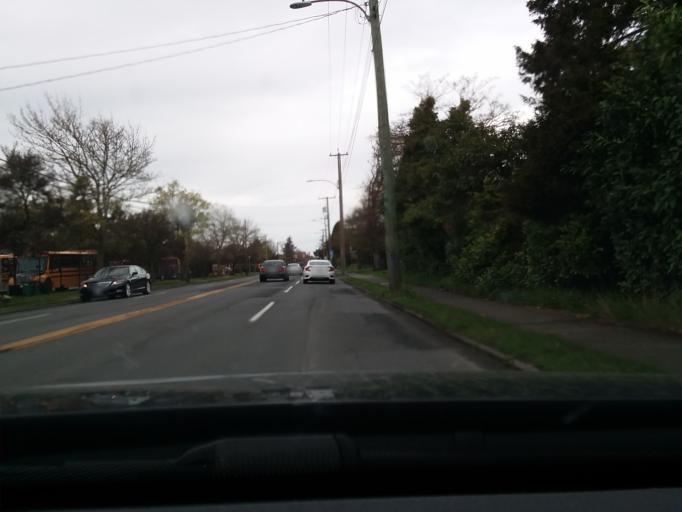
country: CA
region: British Columbia
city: Oak Bay
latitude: 48.4537
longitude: -123.3330
